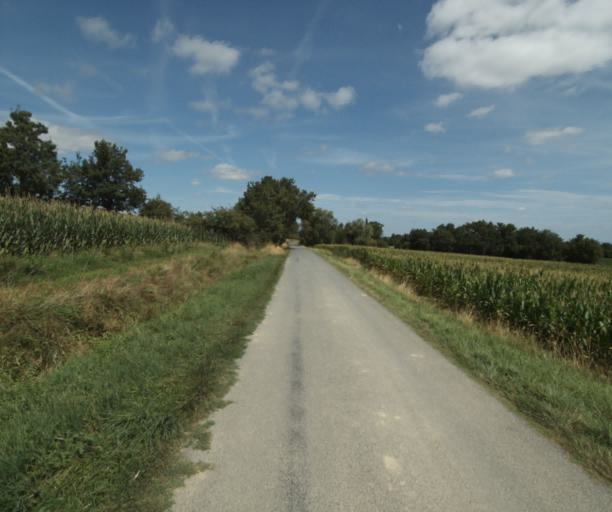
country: FR
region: Midi-Pyrenees
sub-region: Departement du Tarn
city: Soreze
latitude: 43.4842
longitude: 2.0778
